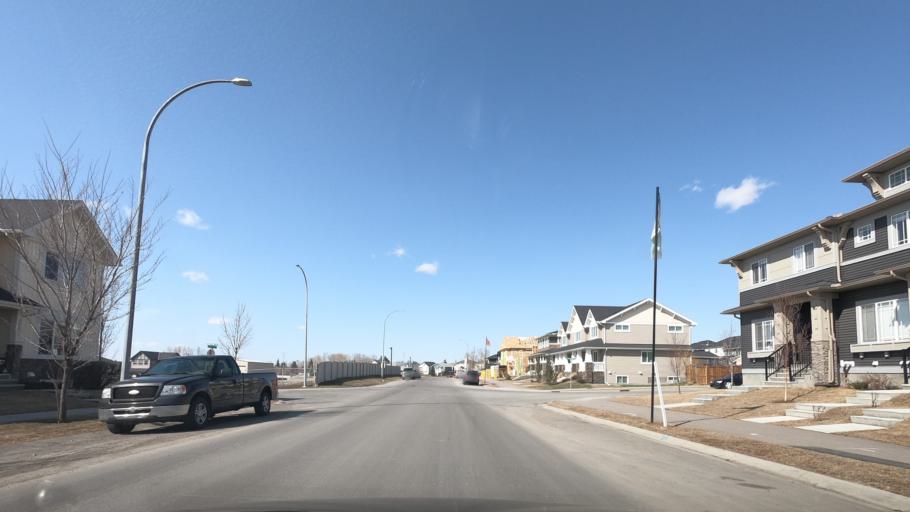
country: CA
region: Alberta
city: Airdrie
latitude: 51.2689
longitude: -113.9817
